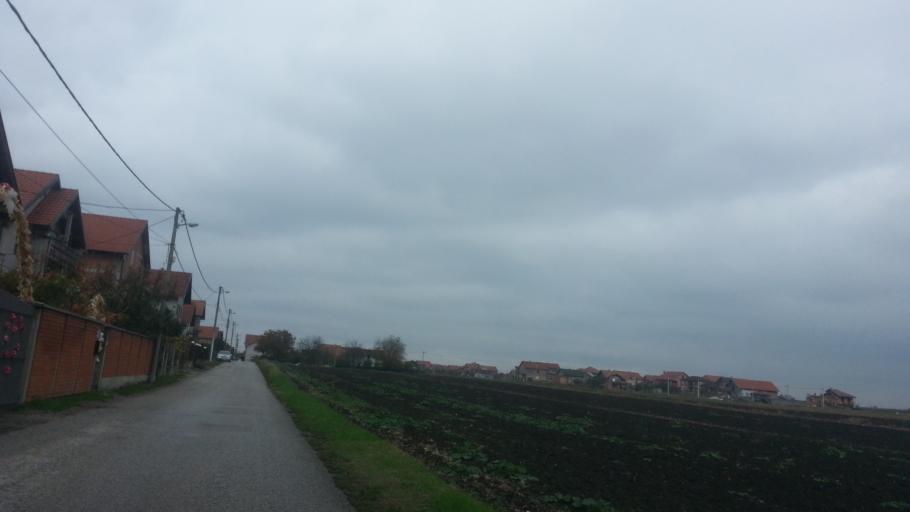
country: RS
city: Novi Banovci
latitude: 44.9001
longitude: 20.2989
